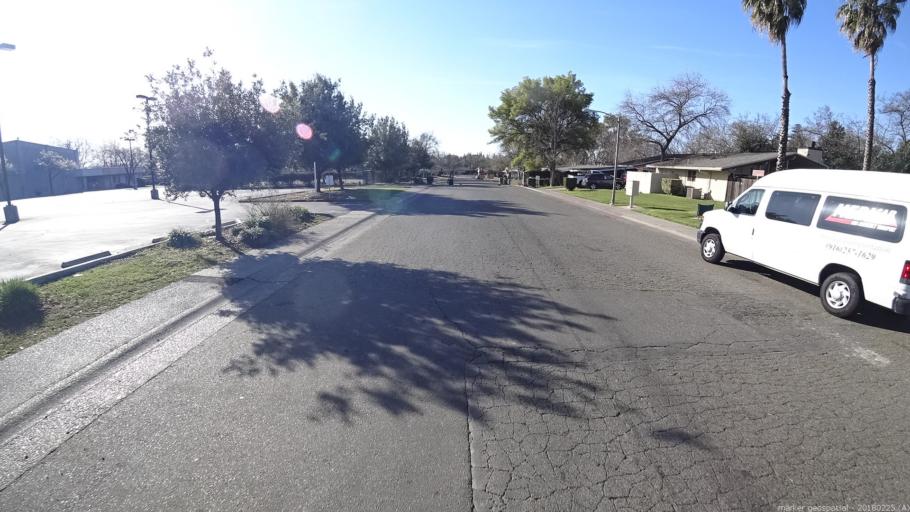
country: US
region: California
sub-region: Sacramento County
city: North Highlands
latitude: 38.7140
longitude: -121.3819
